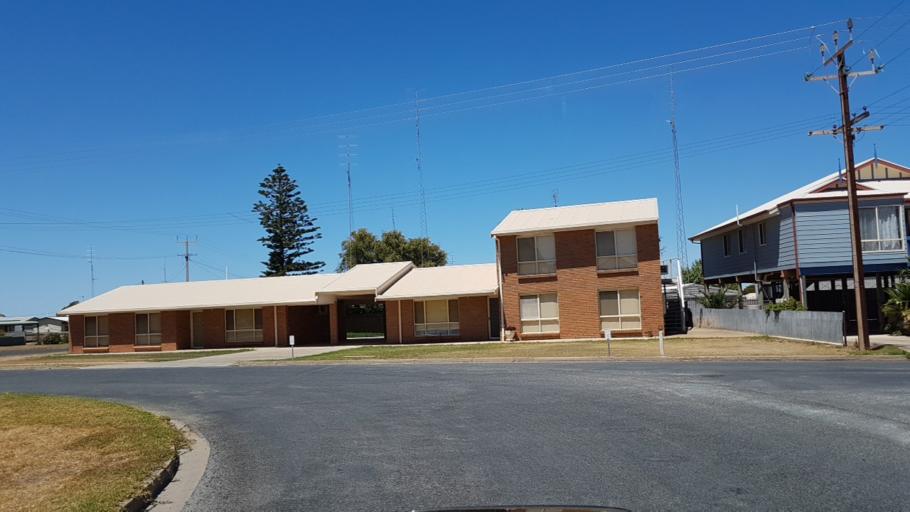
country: AU
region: South Australia
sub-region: Copper Coast
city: Wallaroo
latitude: -33.8966
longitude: 137.6290
